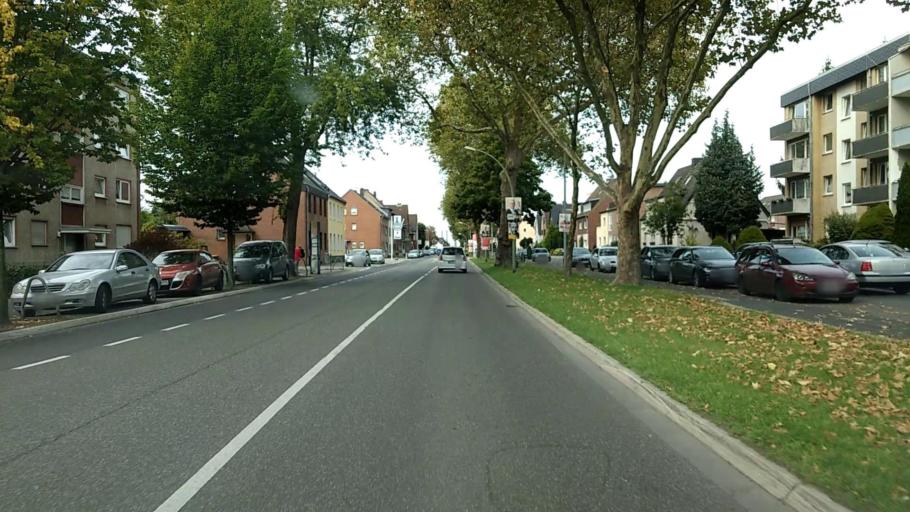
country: DE
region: North Rhine-Westphalia
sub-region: Regierungsbezirk Koln
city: Bergheim
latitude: 50.9373
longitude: 6.6928
